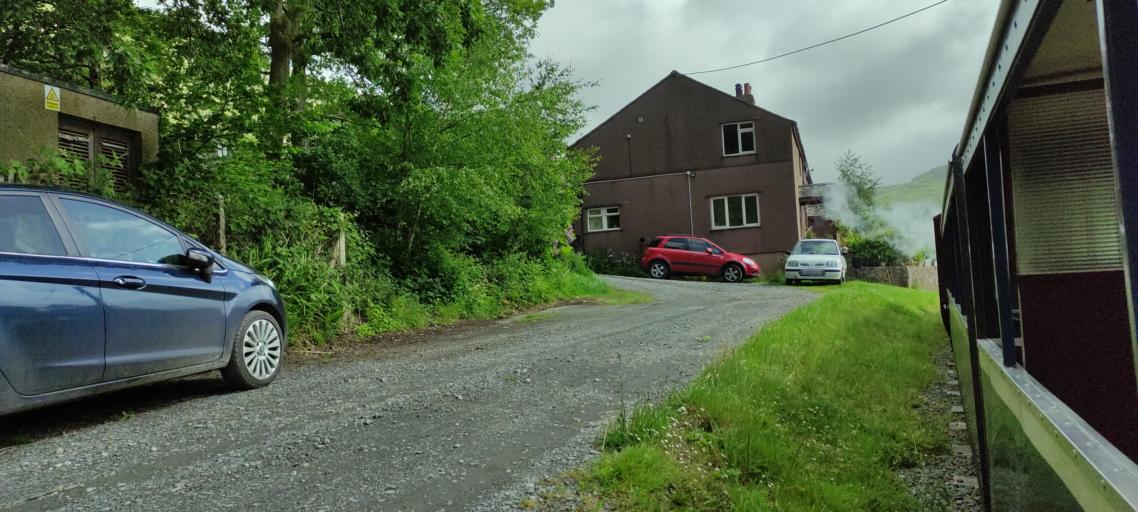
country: GB
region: England
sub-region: Cumbria
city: Millom
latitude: 54.3957
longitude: -3.2778
